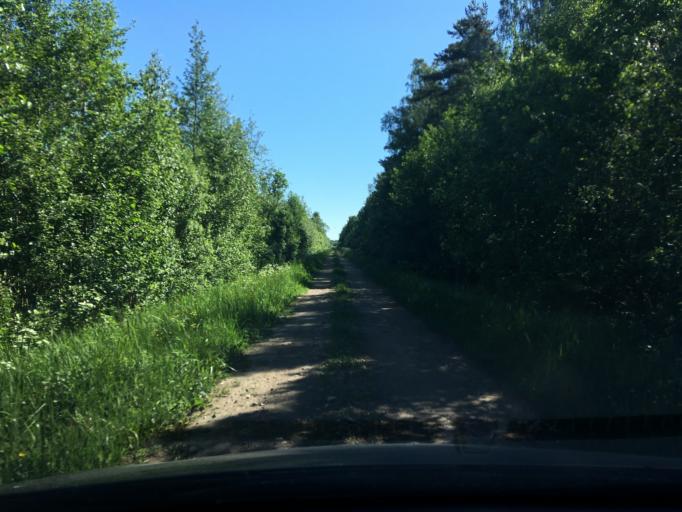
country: EE
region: Laeaene
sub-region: Lihula vald
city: Lihula
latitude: 58.6241
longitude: 23.7161
